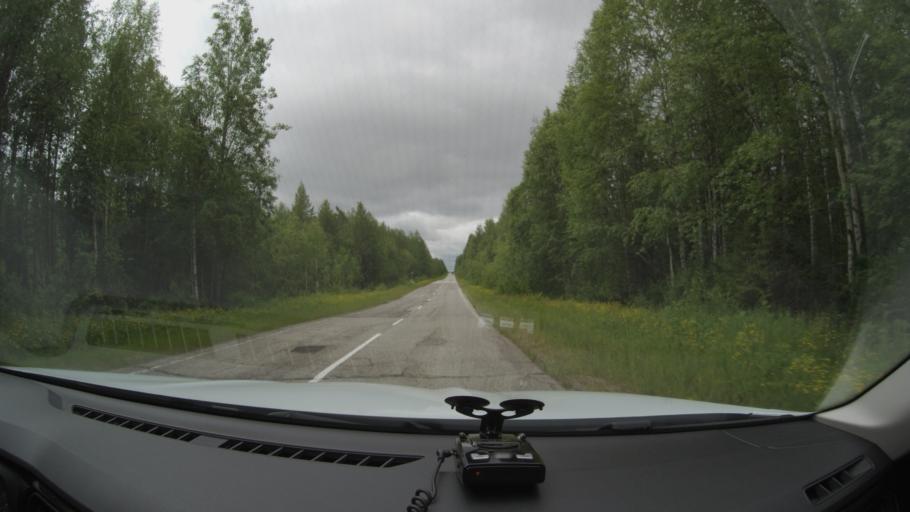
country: RU
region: Komi Republic
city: Nizhniy Odes
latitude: 63.6060
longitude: 54.4969
